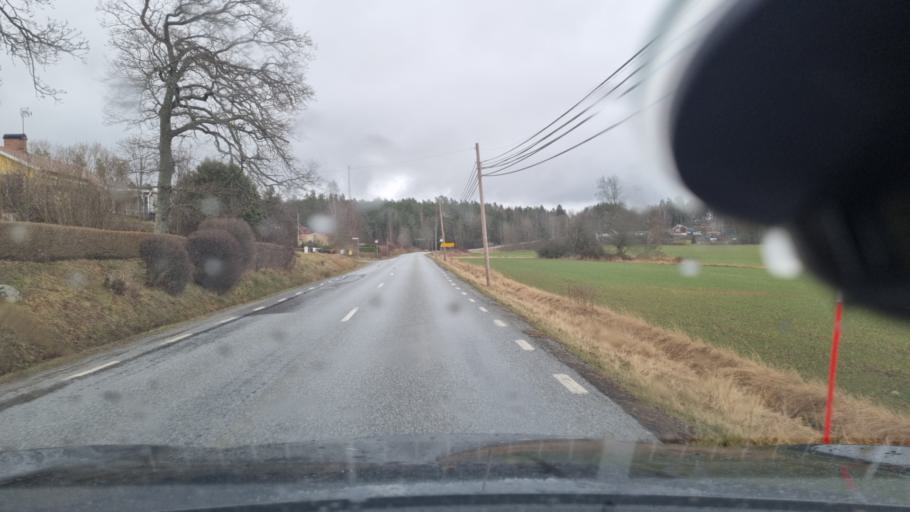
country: SE
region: Stockholm
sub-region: Sigtuna Kommun
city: Sigtuna
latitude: 59.5822
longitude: 17.6720
